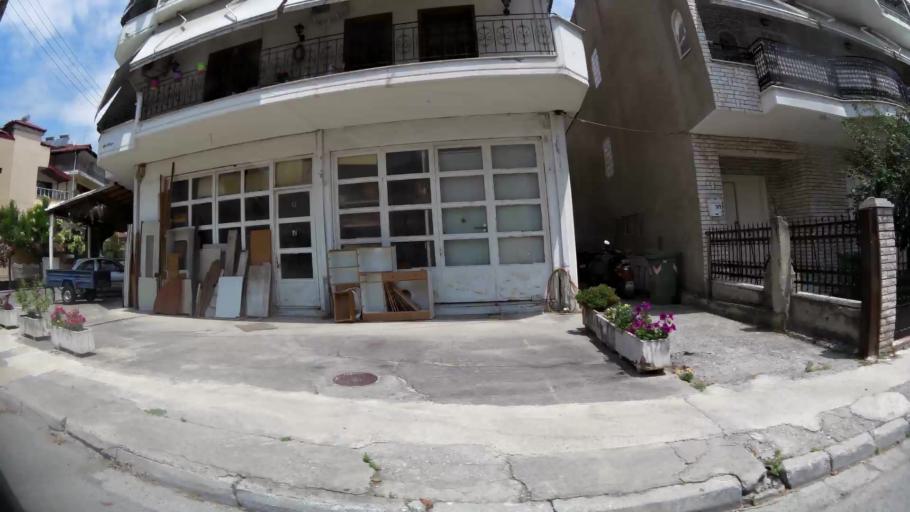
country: GR
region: Central Macedonia
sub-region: Nomos Pierias
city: Katerini
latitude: 40.2668
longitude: 22.5175
